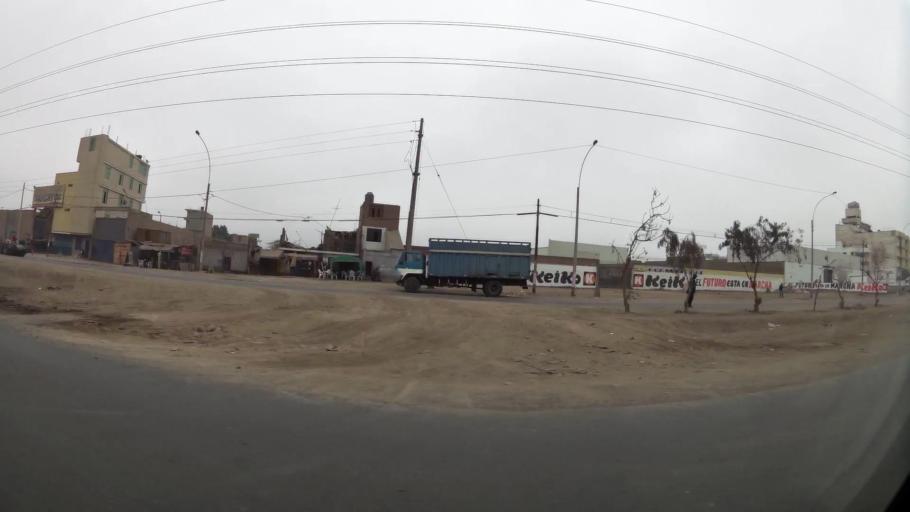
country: PE
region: Lima
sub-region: Lima
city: Urb. Santo Domingo
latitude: -11.9284
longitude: -77.0652
